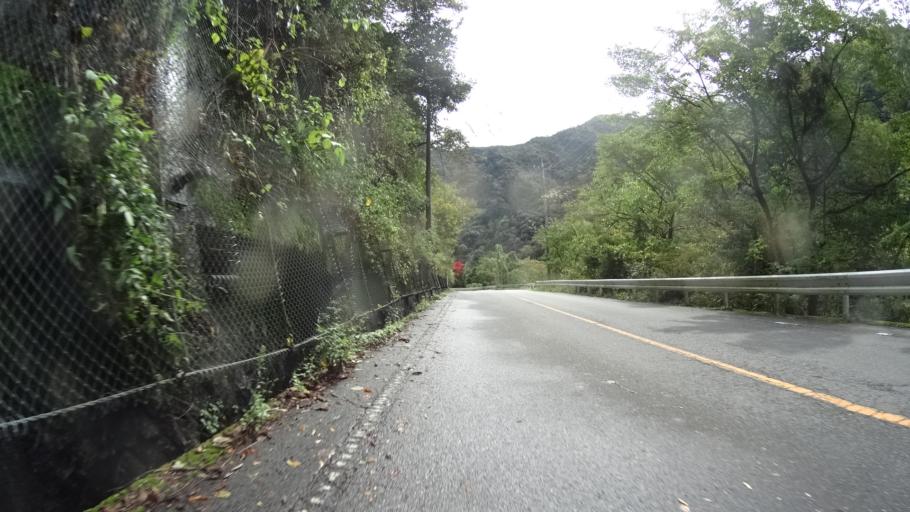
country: JP
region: Yamanashi
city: Otsuki
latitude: 35.7832
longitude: 138.9771
